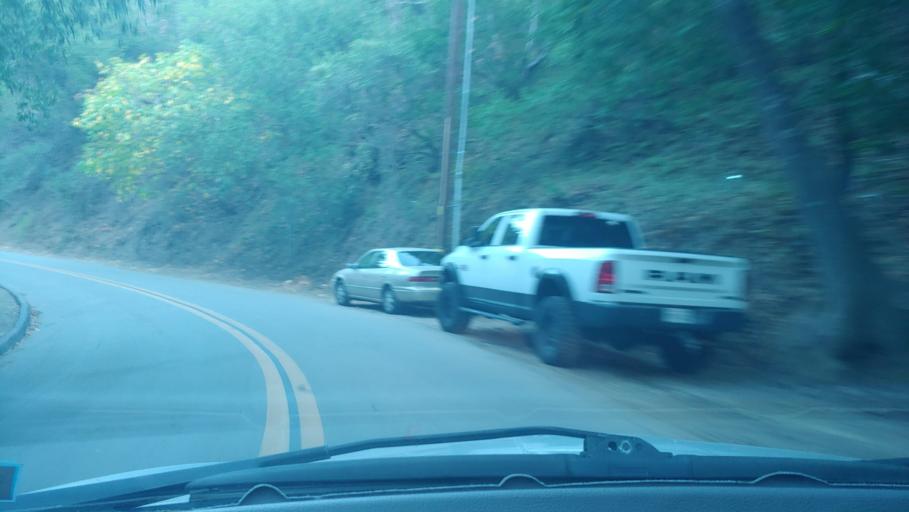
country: US
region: California
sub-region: Santa Barbara County
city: Goleta
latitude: 34.5213
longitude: -119.8399
